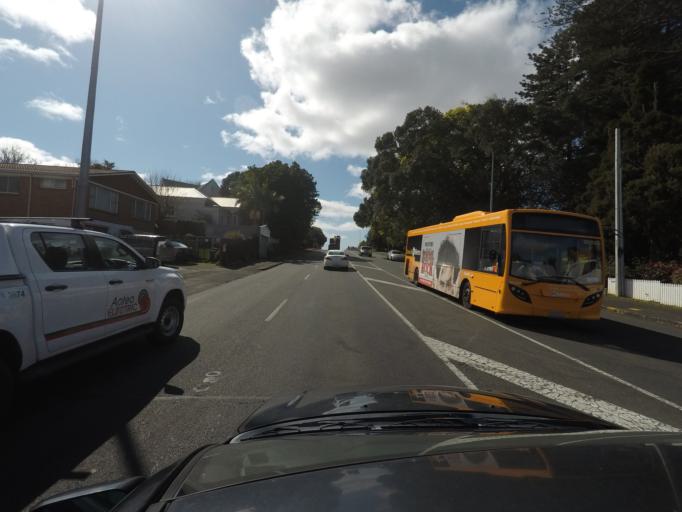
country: NZ
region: Auckland
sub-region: Auckland
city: Rosebank
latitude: -36.8822
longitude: 174.7184
